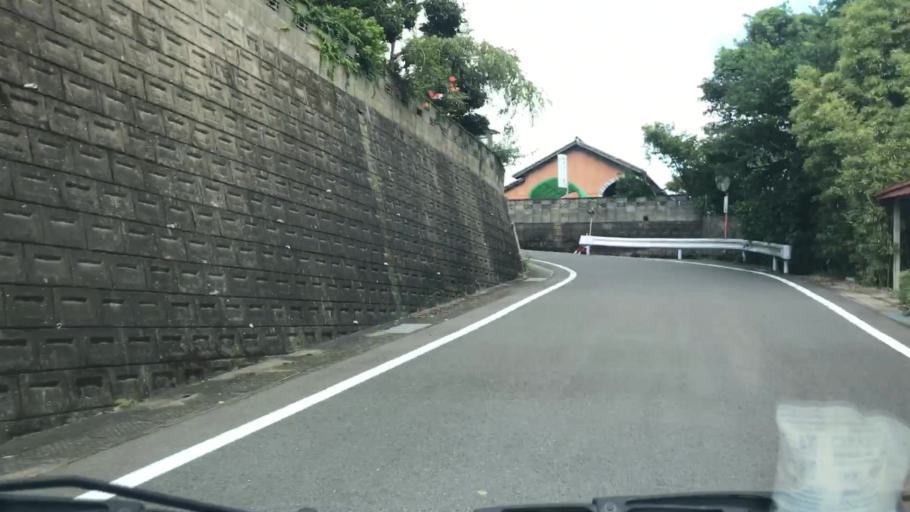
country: JP
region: Saga Prefecture
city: Takeocho-takeo
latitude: 33.2279
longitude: 130.1428
